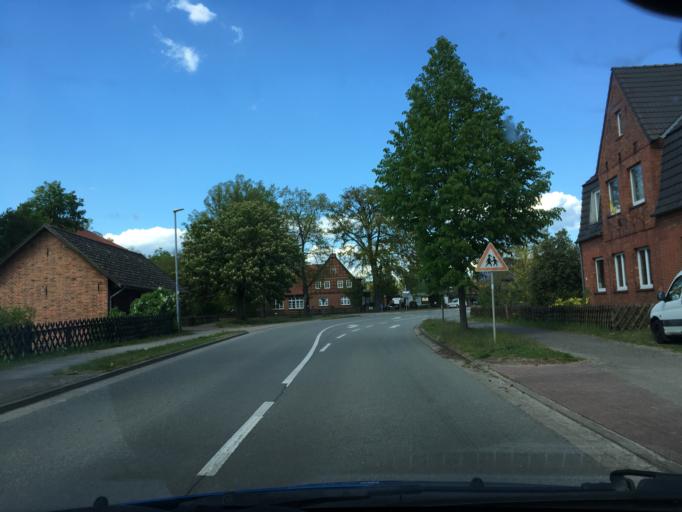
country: DE
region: Lower Saxony
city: Trebel
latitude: 52.9974
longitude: 11.3202
